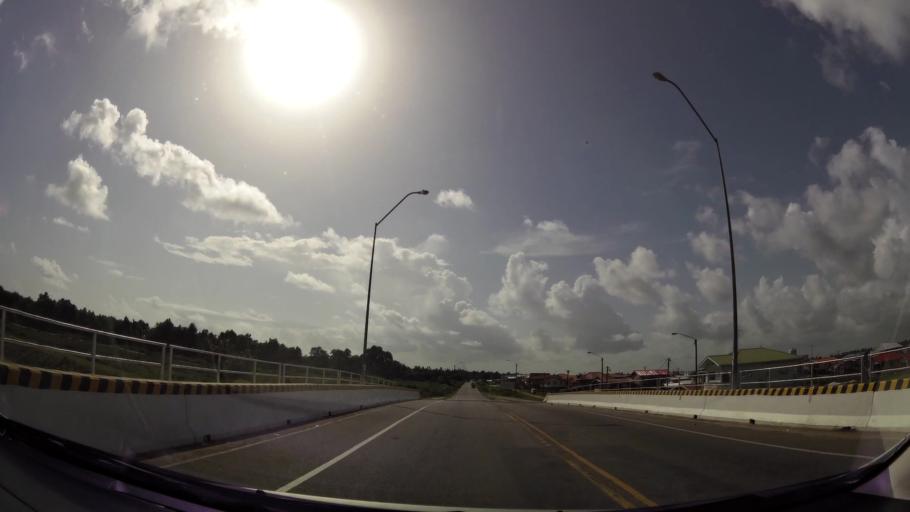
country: GY
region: Demerara-Mahaica
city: Mahaica Village
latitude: 6.7382
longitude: -57.9533
